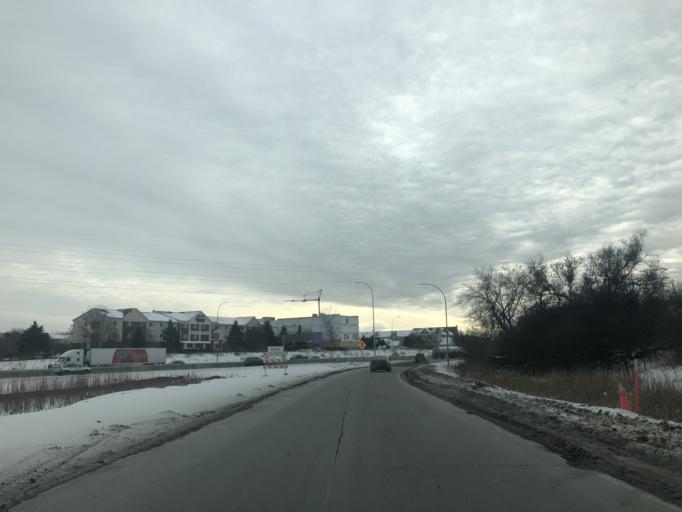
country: US
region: Minnesota
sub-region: Hennepin County
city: Saint Anthony
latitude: 45.0341
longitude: -93.1918
